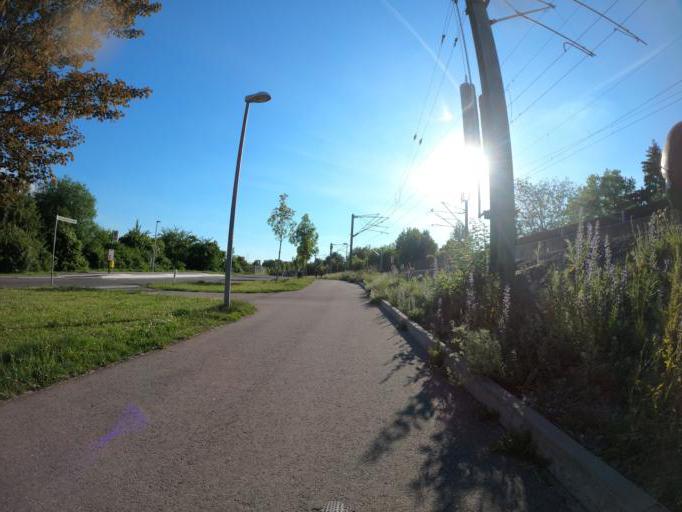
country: DE
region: Baden-Wuerttemberg
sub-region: Regierungsbezirk Stuttgart
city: Magstadt
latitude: 48.7250
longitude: 8.9733
